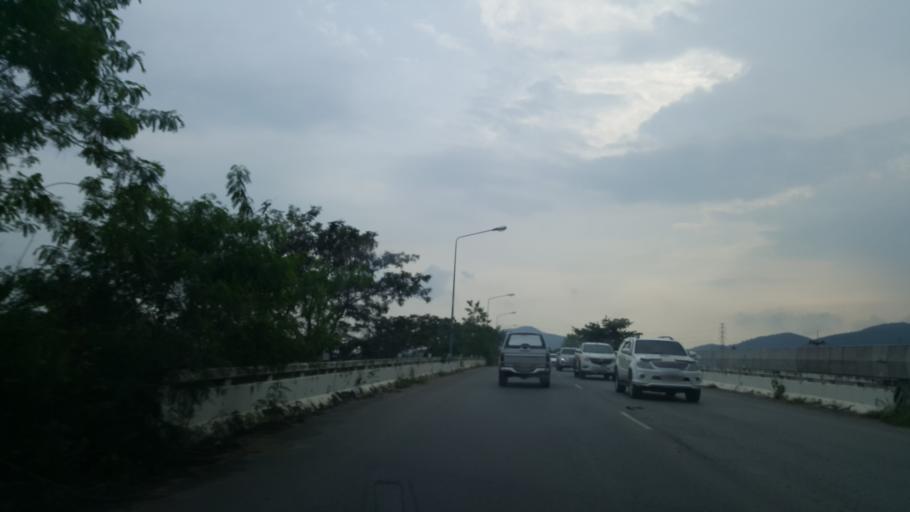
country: TH
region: Rayong
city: Ban Chang
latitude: 12.7330
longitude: 100.9866
